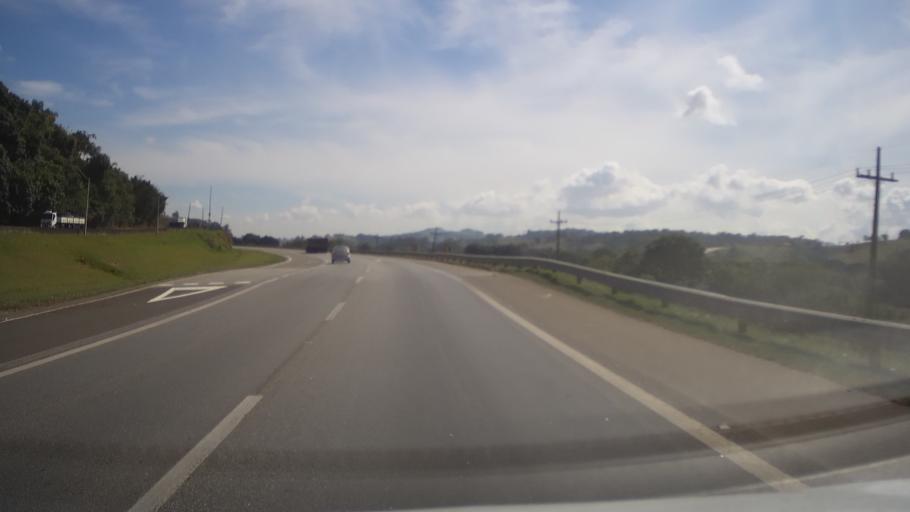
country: BR
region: Minas Gerais
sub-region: Cambui
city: Cambui
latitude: -22.5780
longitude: -46.0437
